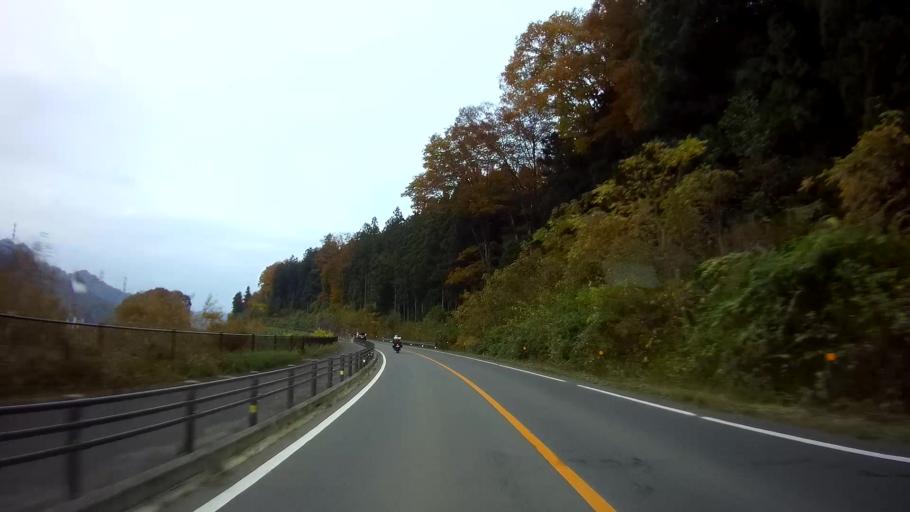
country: JP
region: Gunma
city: Nakanojomachi
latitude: 36.5670
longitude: 138.7361
